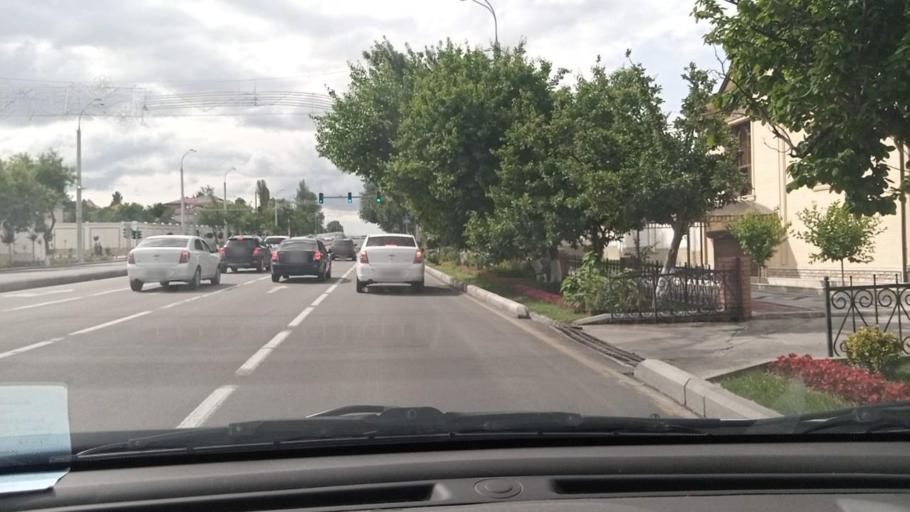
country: UZ
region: Toshkent
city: Salor
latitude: 41.3286
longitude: 69.3557
